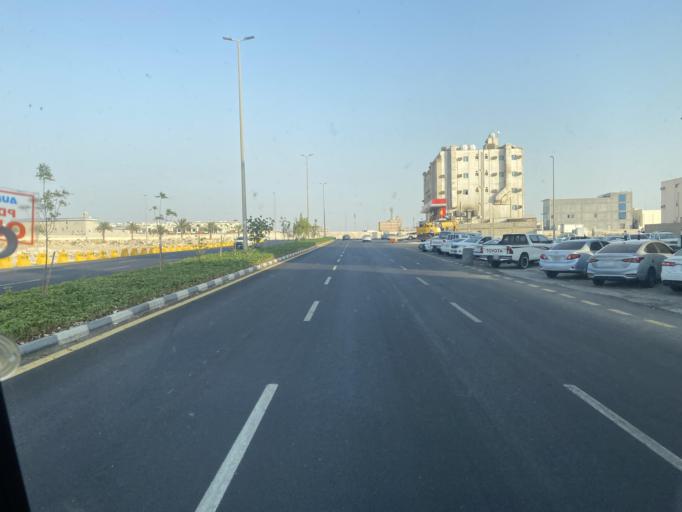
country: SA
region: Eastern Province
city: Dhahran
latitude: 26.3517
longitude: 50.0503
